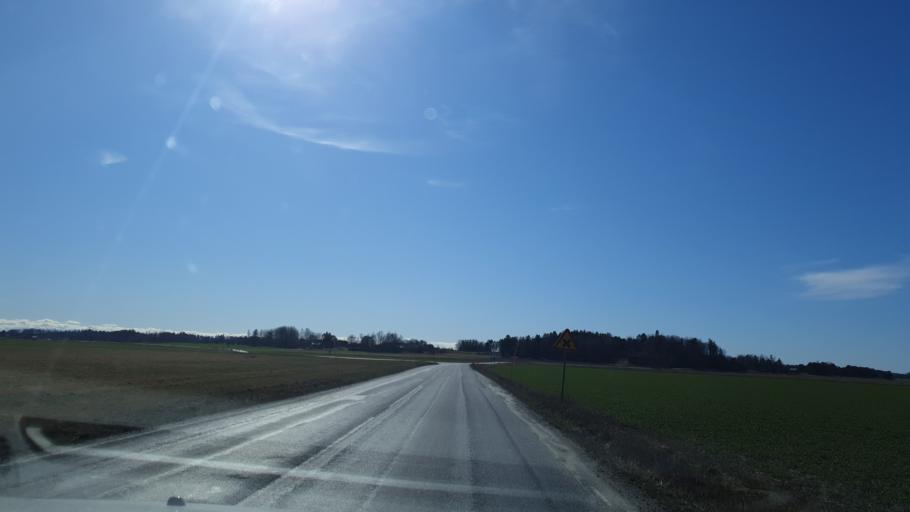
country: SE
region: Uppsala
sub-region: Enkopings Kommun
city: Grillby
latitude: 59.6041
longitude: 17.2737
